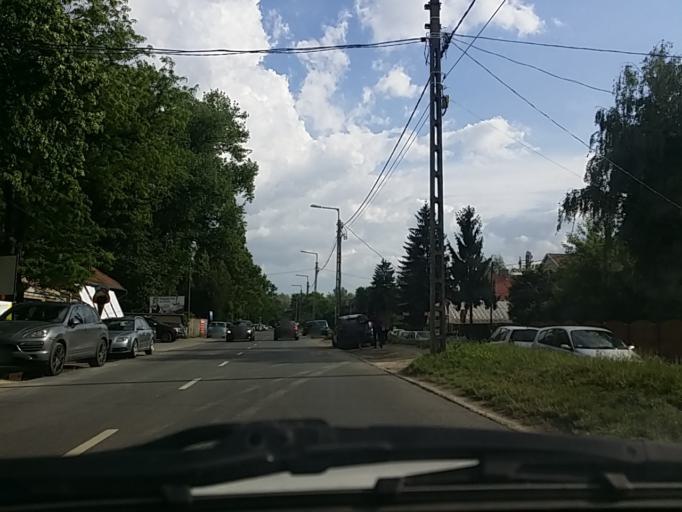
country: HU
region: Budapest
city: Budapest IV. keruelet
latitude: 47.5721
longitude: 19.0619
